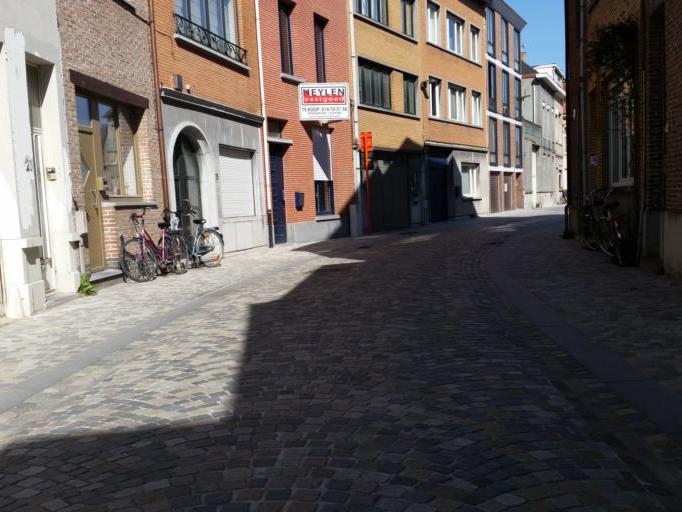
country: BE
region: Flanders
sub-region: Provincie Antwerpen
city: Mechelen
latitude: 51.0259
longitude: 4.4839
